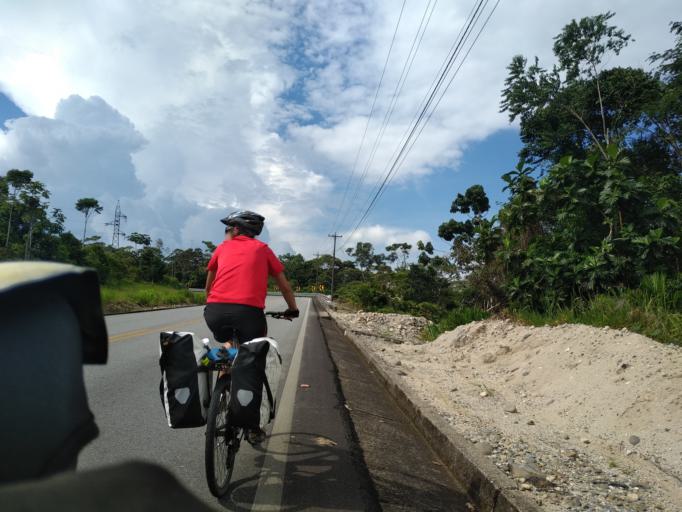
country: EC
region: Napo
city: Tena
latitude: -1.0895
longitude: -77.7895
